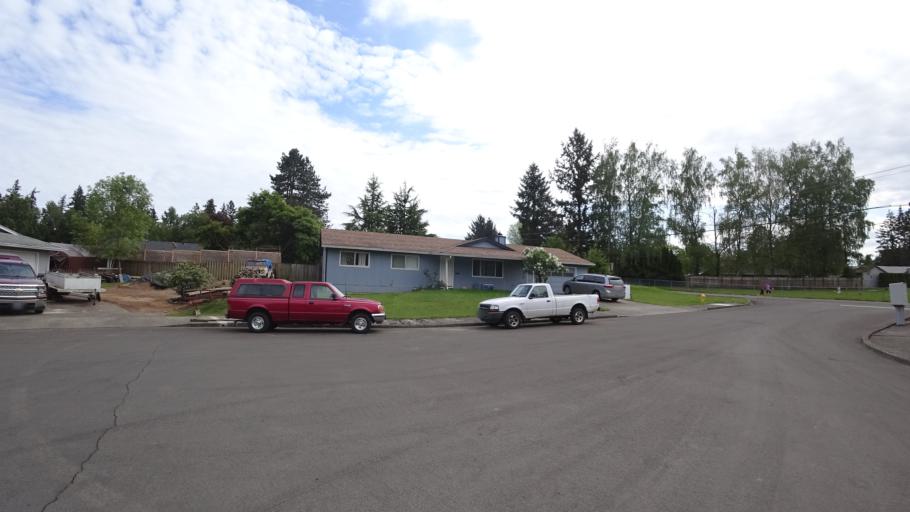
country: US
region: Oregon
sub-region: Washington County
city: Hillsboro
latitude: 45.4950
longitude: -122.9527
